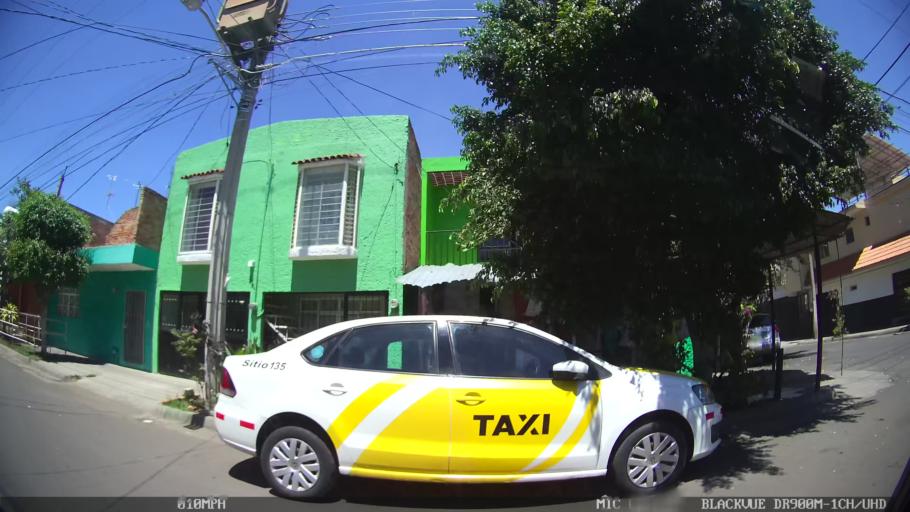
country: MX
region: Jalisco
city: Tlaquepaque
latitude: 20.6670
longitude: -103.2743
